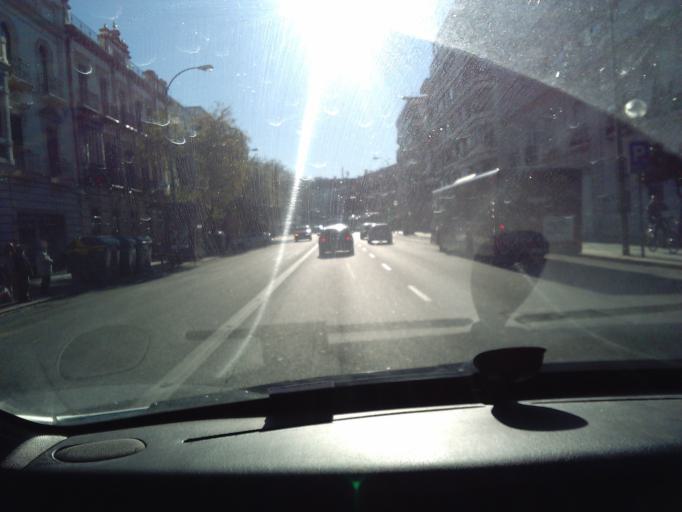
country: ES
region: Andalusia
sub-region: Provincia de Sevilla
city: Sevilla
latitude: 37.3953
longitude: -5.9829
